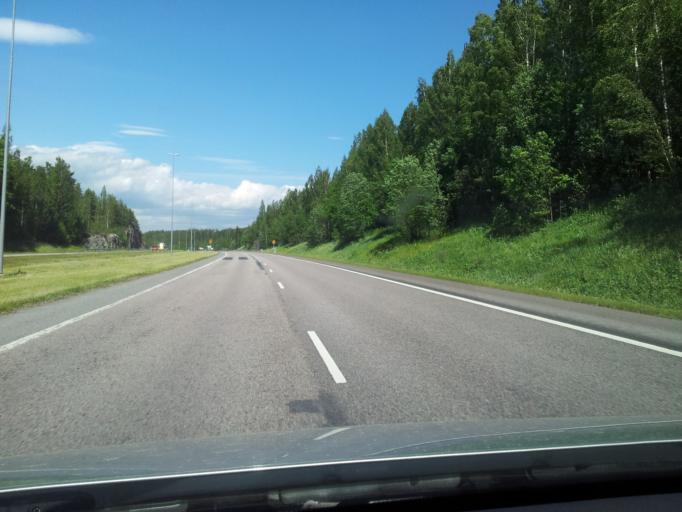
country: FI
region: Uusimaa
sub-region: Porvoo
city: Porvoo
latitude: 60.3388
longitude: 25.5039
